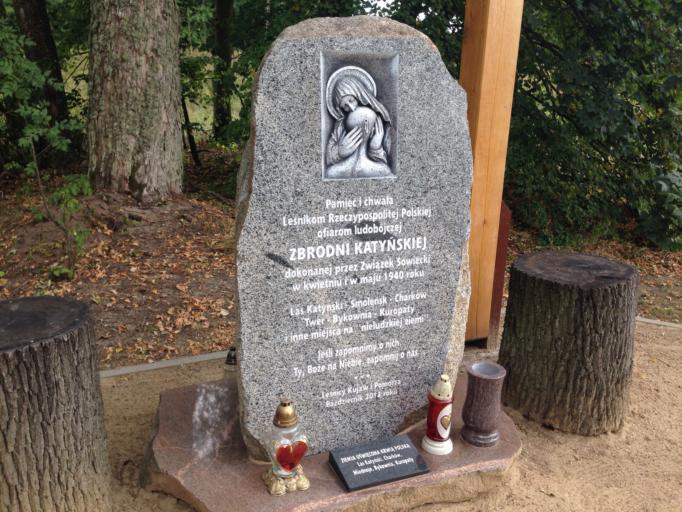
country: PL
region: Kujawsko-Pomorskie
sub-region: Powiat tucholski
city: Lubiewo
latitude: 53.5167
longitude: 18.1106
